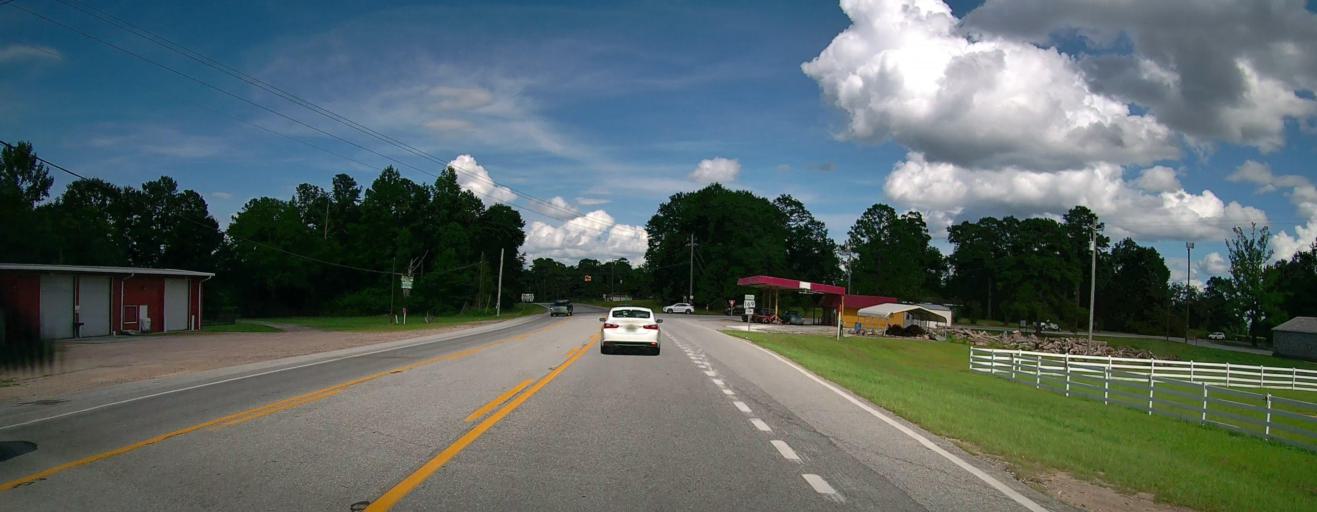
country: US
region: Alabama
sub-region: Russell County
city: Ladonia
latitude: 32.4567
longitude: -85.1880
